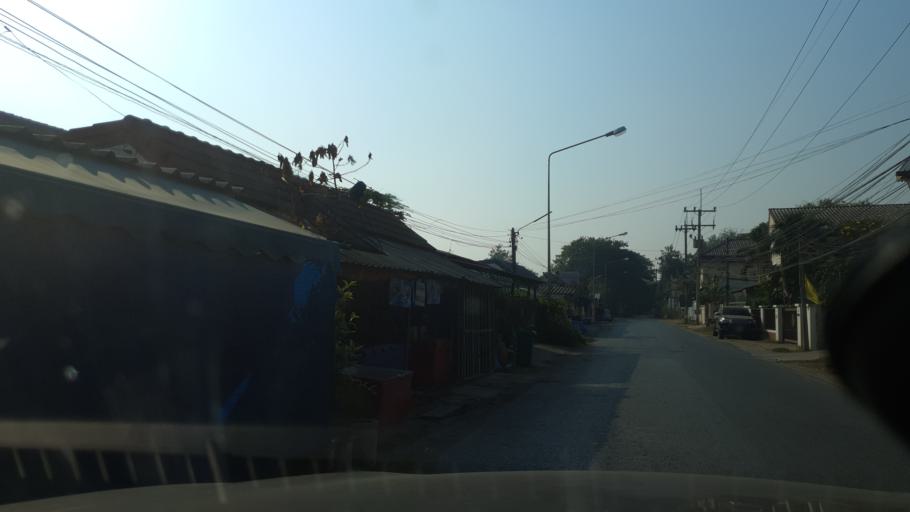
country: TH
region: Phra Nakhon Si Ayutthaya
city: Phra Nakhon Si Ayutthaya
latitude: 14.3643
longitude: 100.5604
